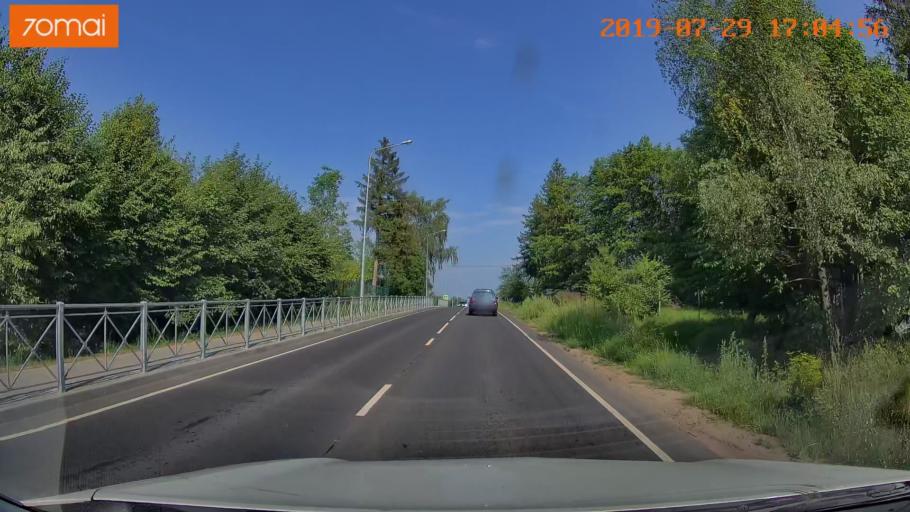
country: RU
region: Kaliningrad
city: Vzmorye
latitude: 54.8181
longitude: 20.2851
